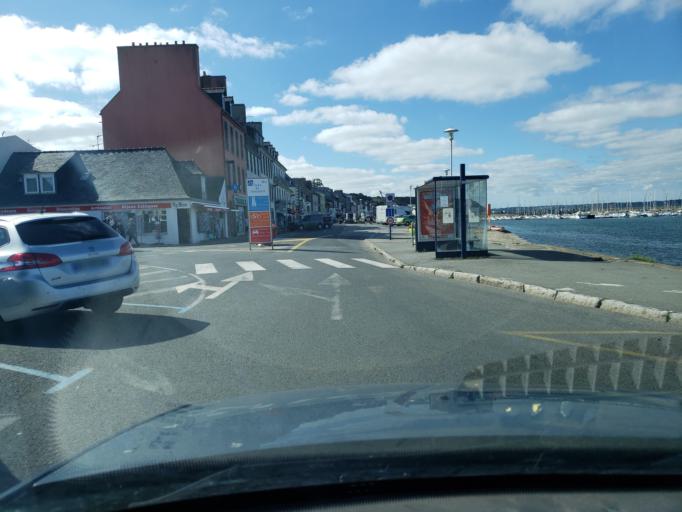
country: FR
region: Brittany
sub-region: Departement du Finistere
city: Camaret-sur-Mer
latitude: 48.2761
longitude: -4.5951
